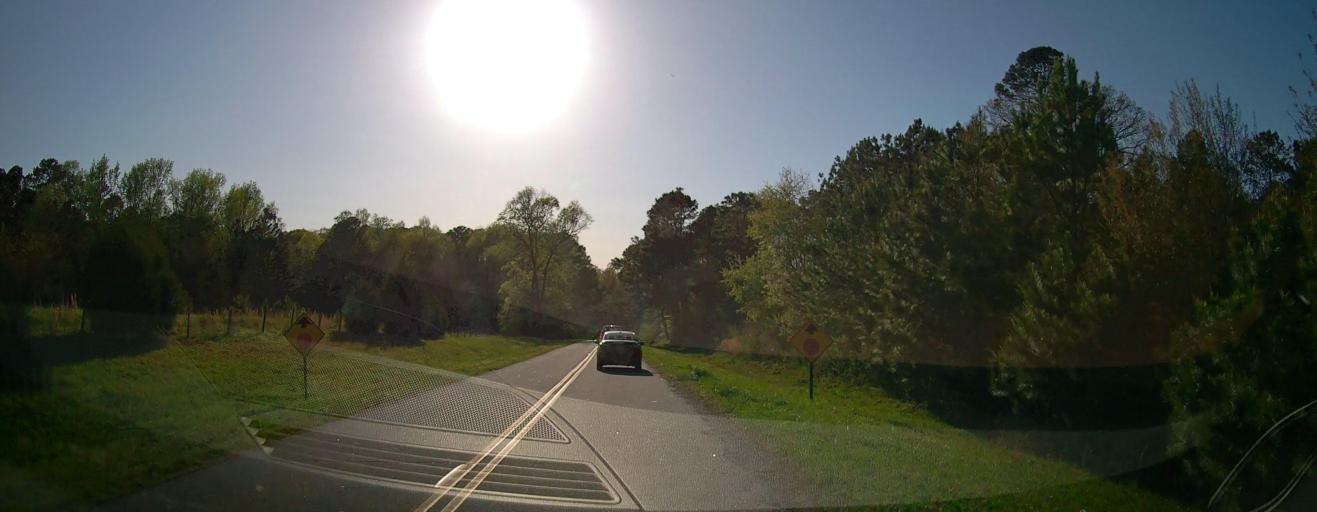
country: US
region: Georgia
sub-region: Butts County
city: Jackson
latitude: 33.3085
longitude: -83.9008
